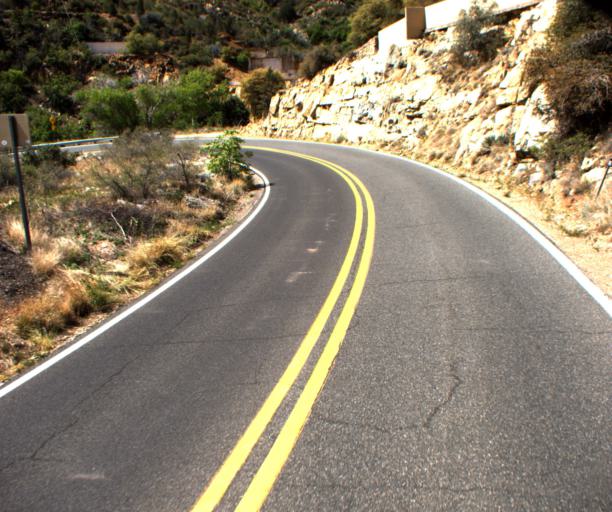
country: US
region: Arizona
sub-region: Yavapai County
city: Clarkdale
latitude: 34.7405
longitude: -112.1239
